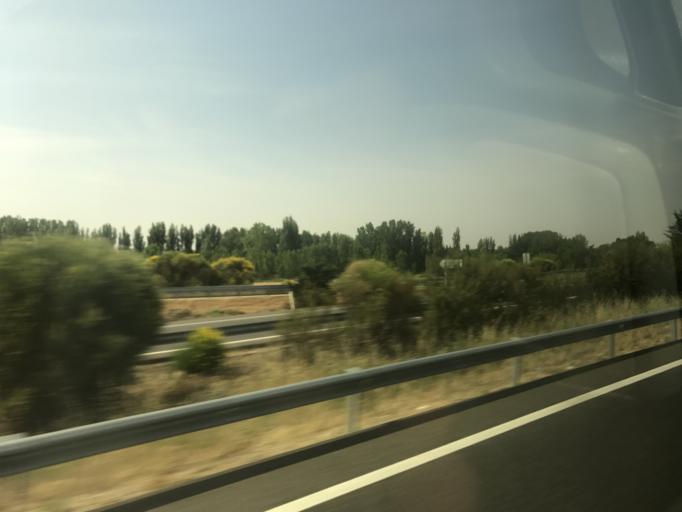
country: ES
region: Castille and Leon
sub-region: Provincia de Palencia
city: Quintana del Puente
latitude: 42.0997
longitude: -4.1989
